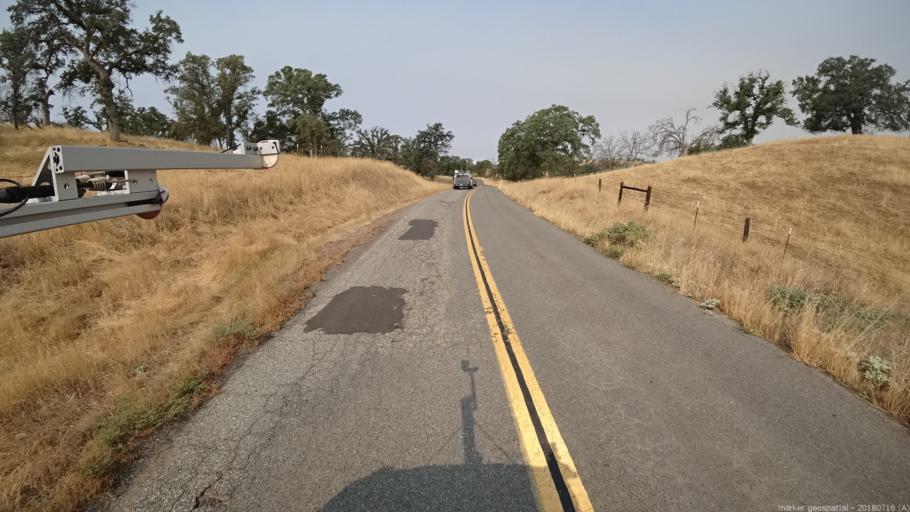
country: US
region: California
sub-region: Madera County
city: Yosemite Lakes
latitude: 37.1222
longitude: -119.8630
